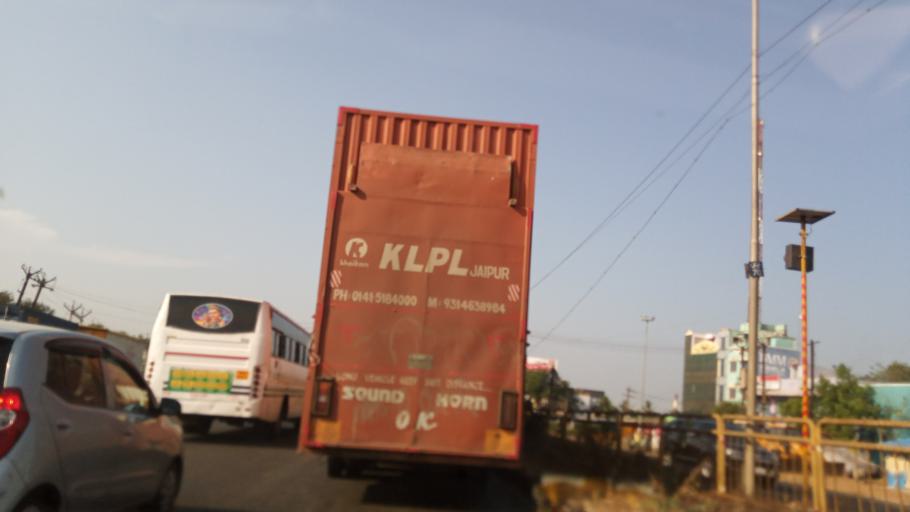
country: IN
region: Tamil Nadu
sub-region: Kancheepuram
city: Sriperumbudur
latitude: 12.9965
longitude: 79.9893
